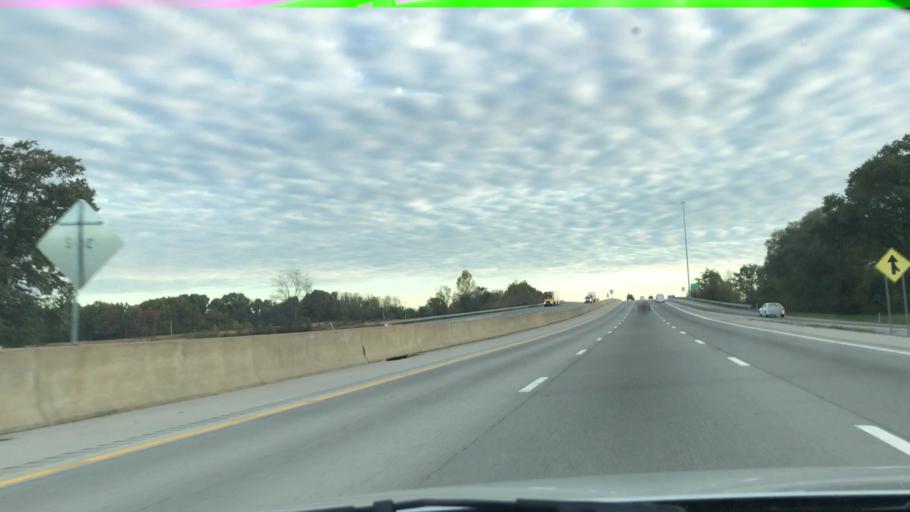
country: US
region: Kentucky
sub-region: Simpson County
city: Franklin
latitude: 36.6676
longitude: -86.5542
